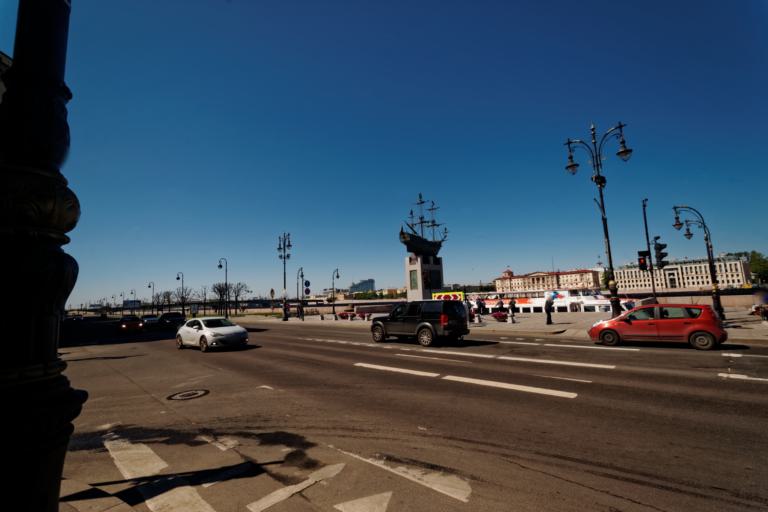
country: RU
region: St.-Petersburg
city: Centralniy
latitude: 59.9496
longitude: 30.3598
